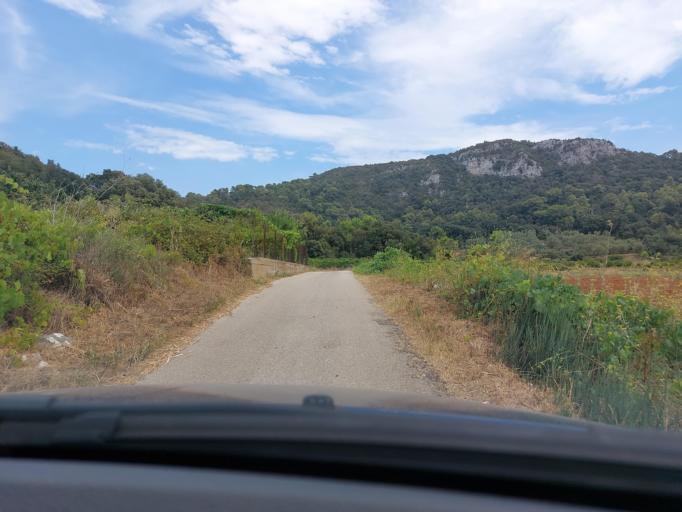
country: HR
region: Dubrovacko-Neretvanska
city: Smokvica
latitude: 42.7552
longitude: 16.9206
